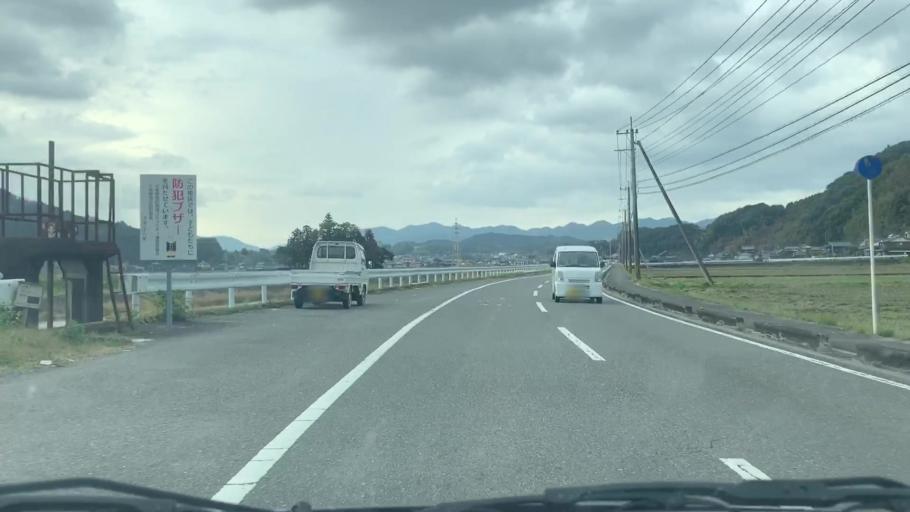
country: JP
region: Saga Prefecture
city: Ureshinomachi-shimojuku
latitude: 33.1339
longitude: 130.0136
